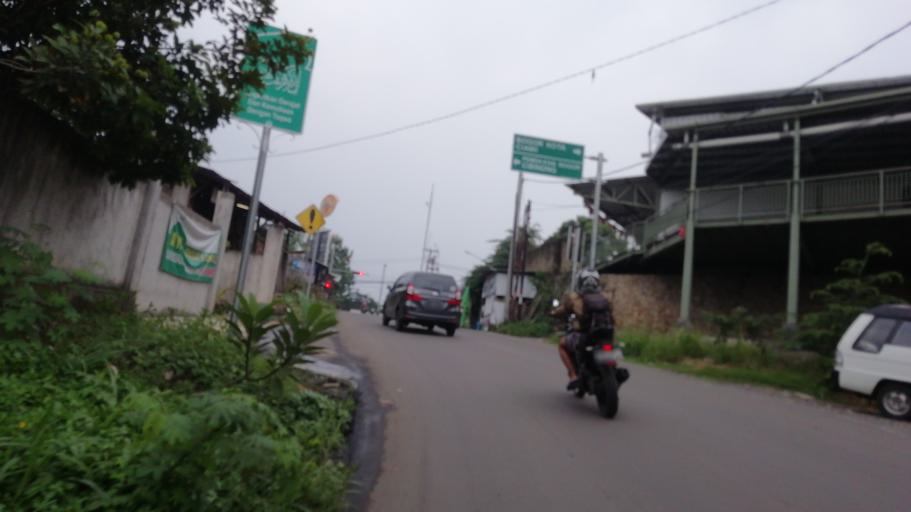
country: ID
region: West Java
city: Bogor
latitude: -6.5334
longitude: 106.8062
